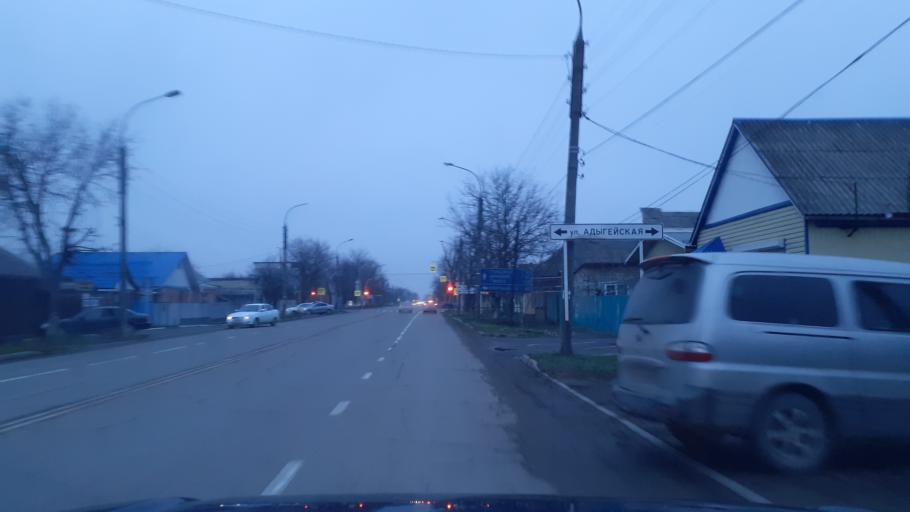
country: RU
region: Adygeya
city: Maykop
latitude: 44.6189
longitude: 40.0936
